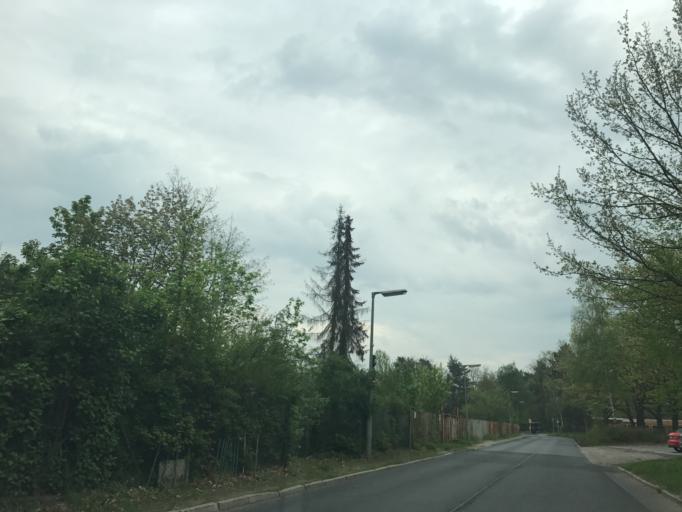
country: DE
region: Berlin
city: Falkenhagener Feld
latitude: 52.5645
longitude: 13.1600
